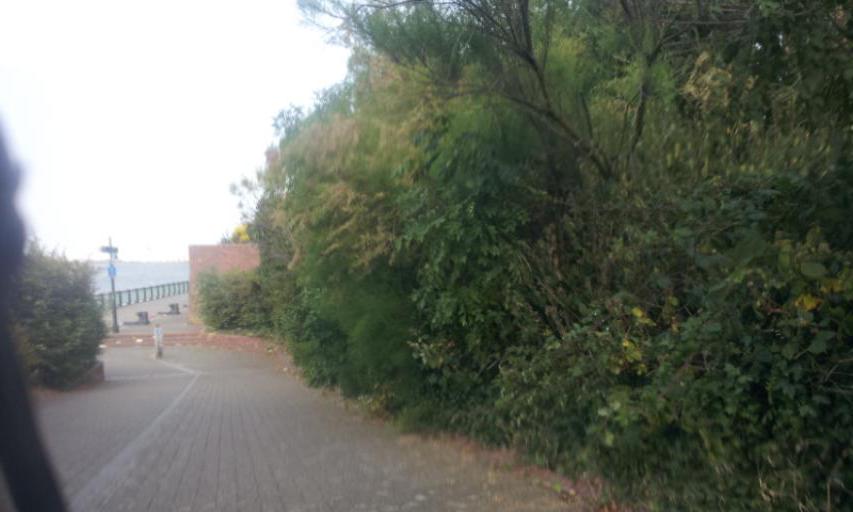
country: GB
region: England
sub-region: Greater London
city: Abbey Wood
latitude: 51.5097
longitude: 0.1113
